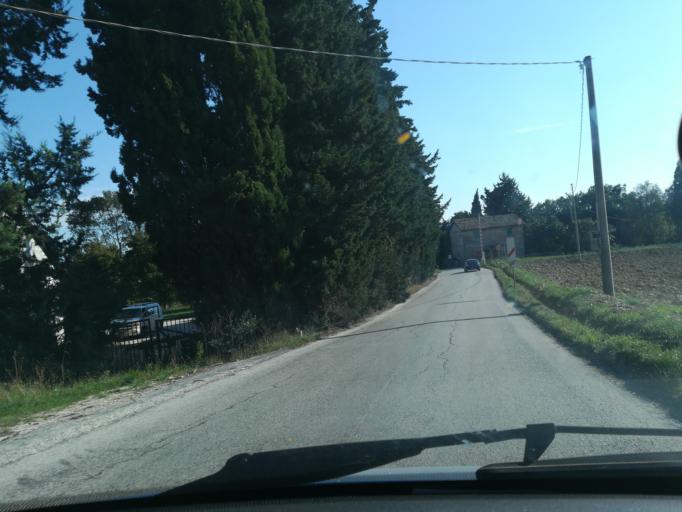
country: IT
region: The Marches
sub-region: Provincia di Macerata
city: Piediripa
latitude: 43.2869
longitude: 13.4881
